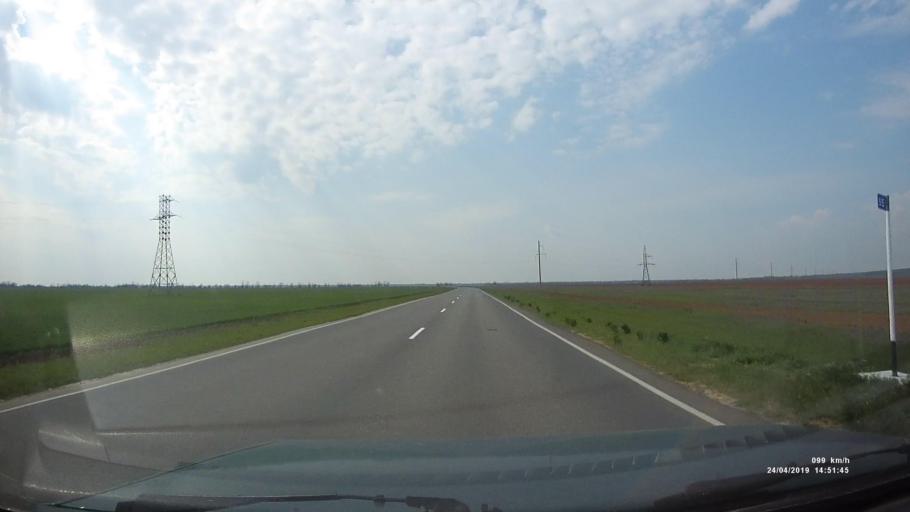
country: RU
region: Rostov
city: Remontnoye
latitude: 46.5272
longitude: 43.6948
